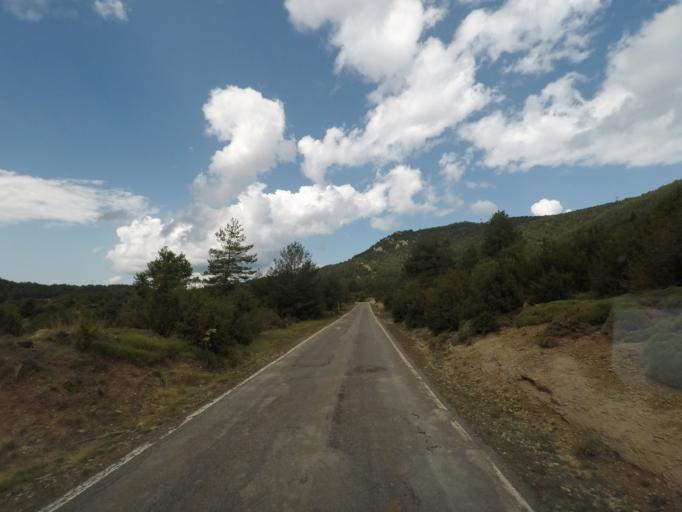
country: ES
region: Aragon
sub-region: Provincia de Huesca
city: Fiscal
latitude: 42.4021
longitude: -0.0557
